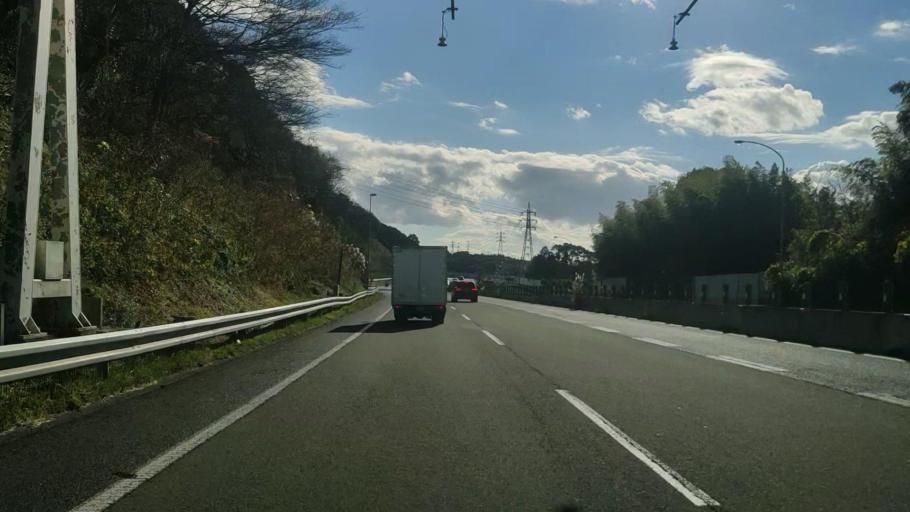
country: JP
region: Fukuoka
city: Kitakyushu
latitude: 33.8483
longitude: 130.7669
